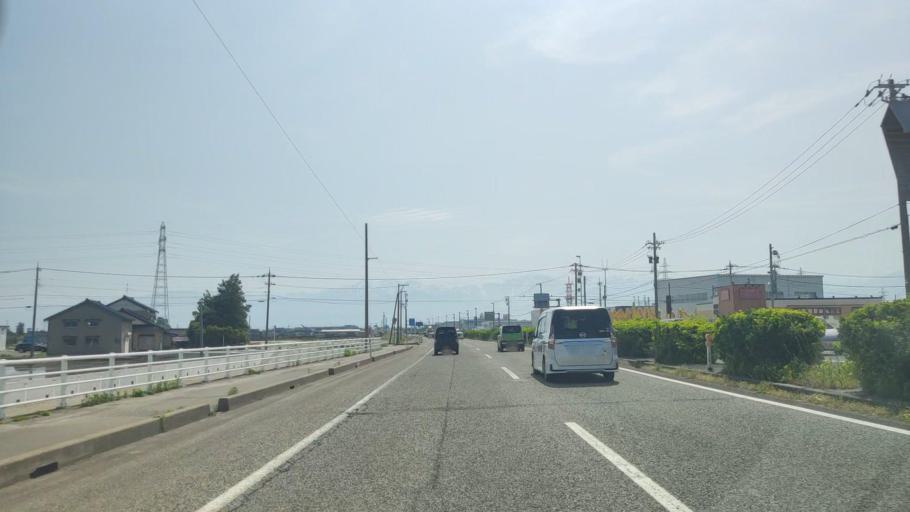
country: JP
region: Toyama
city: Toyama-shi
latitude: 36.7212
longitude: 137.2520
